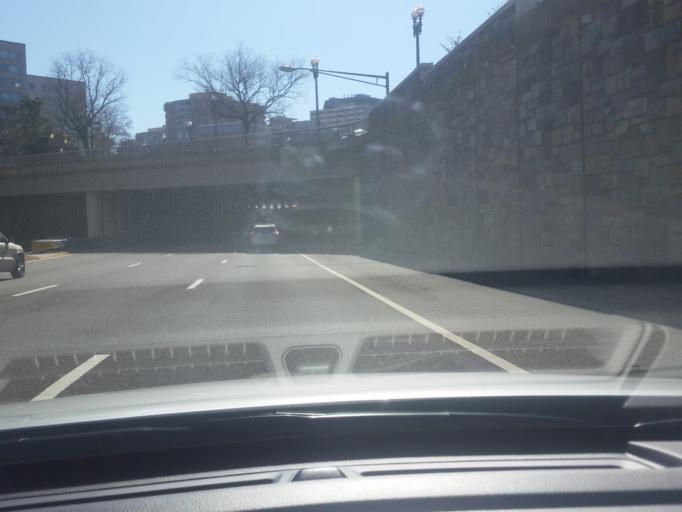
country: US
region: Washington, D.C.
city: Washington, D.C.
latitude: 38.8998
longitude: -77.0544
